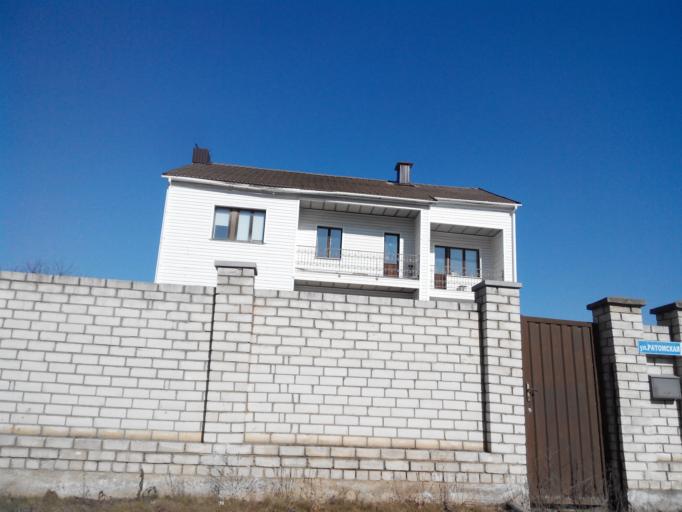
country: BY
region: Minsk
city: Zhdanovichy
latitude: 53.9152
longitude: 27.3967
